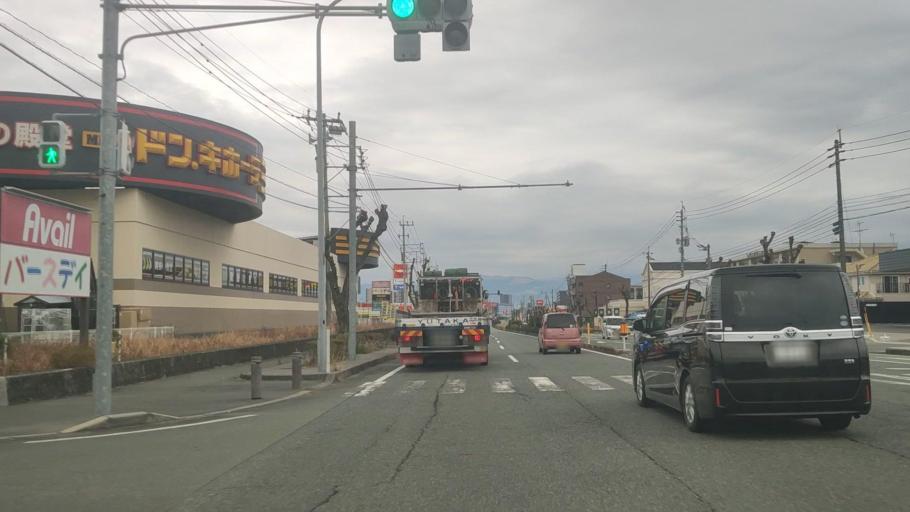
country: JP
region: Kumamoto
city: Ozu
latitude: 32.8610
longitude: 130.8058
